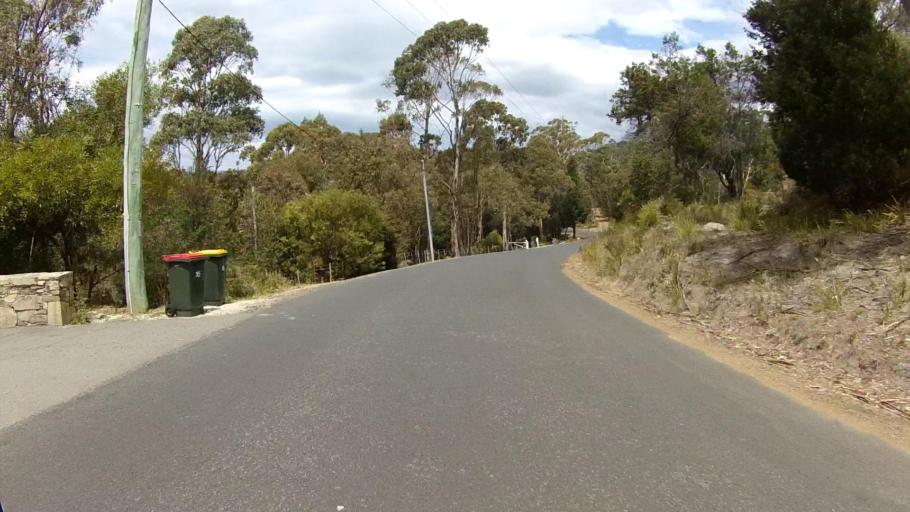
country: AU
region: Tasmania
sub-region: Sorell
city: Sorell
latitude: -42.5890
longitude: 147.9149
